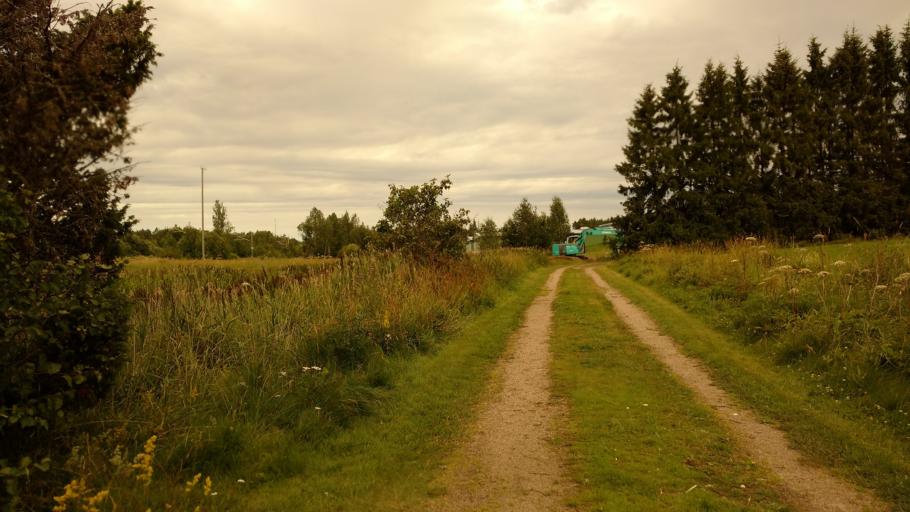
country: FI
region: Varsinais-Suomi
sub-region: Turku
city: Piikkioe
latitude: 60.4317
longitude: 22.4678
